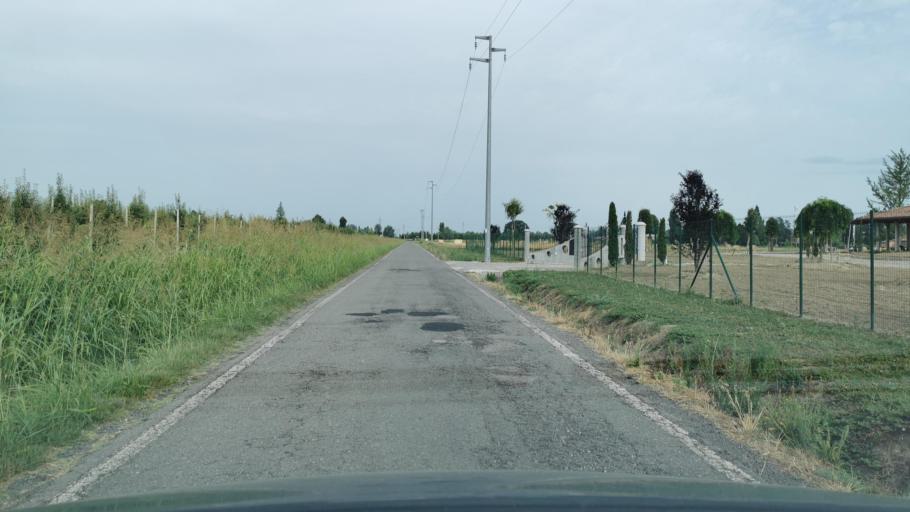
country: IT
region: Emilia-Romagna
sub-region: Provincia di Modena
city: Villanova
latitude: 44.6871
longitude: 10.9034
